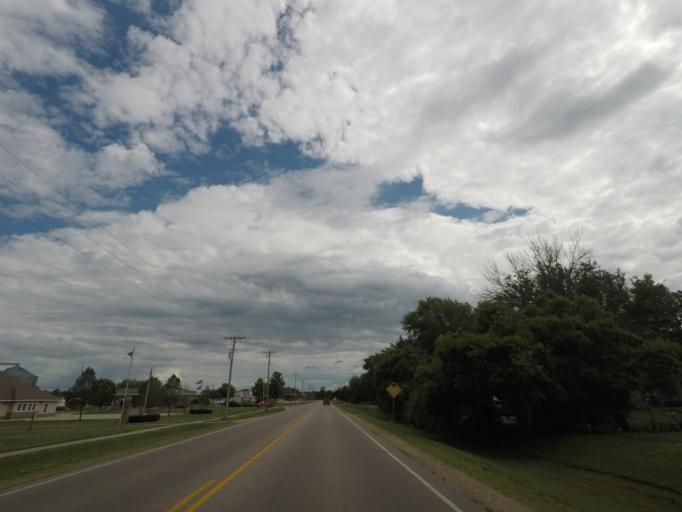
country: US
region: Wisconsin
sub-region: Dane County
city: Belleville
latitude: 42.8707
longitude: -89.5330
